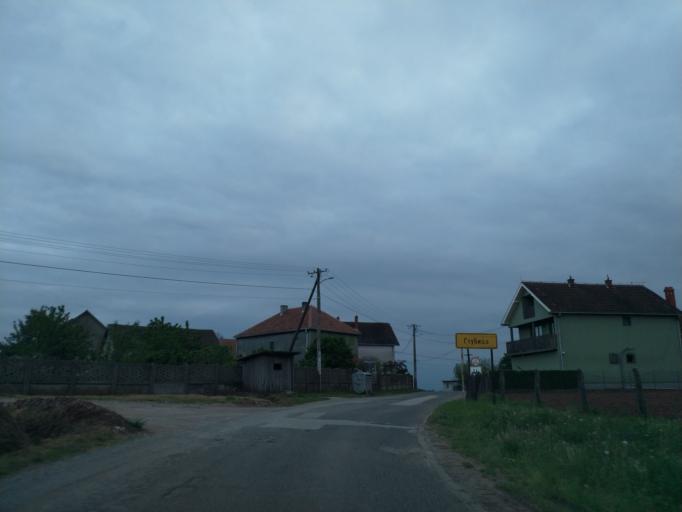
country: RS
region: Central Serbia
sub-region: Pomoravski Okrug
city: Paracin
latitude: 43.9470
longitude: 21.4928
